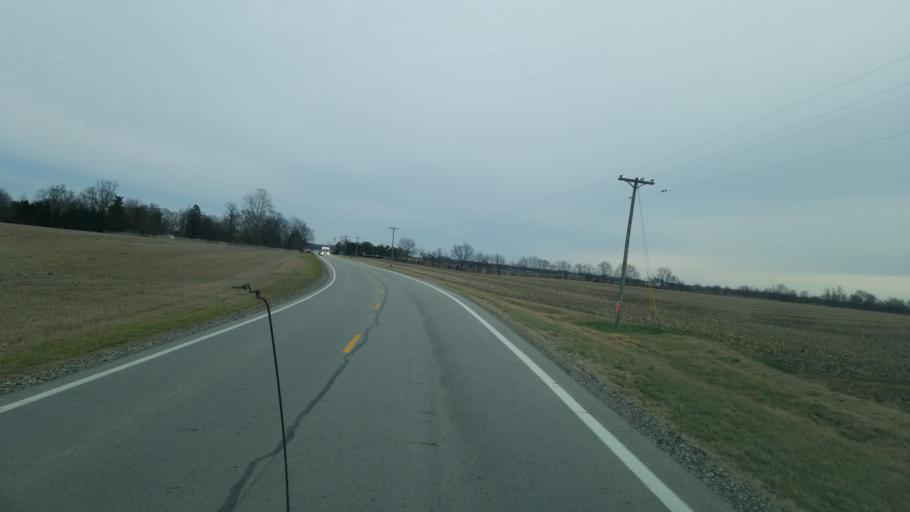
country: US
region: Ohio
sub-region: Pickaway County
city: Circleville
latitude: 39.6085
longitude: -82.9997
